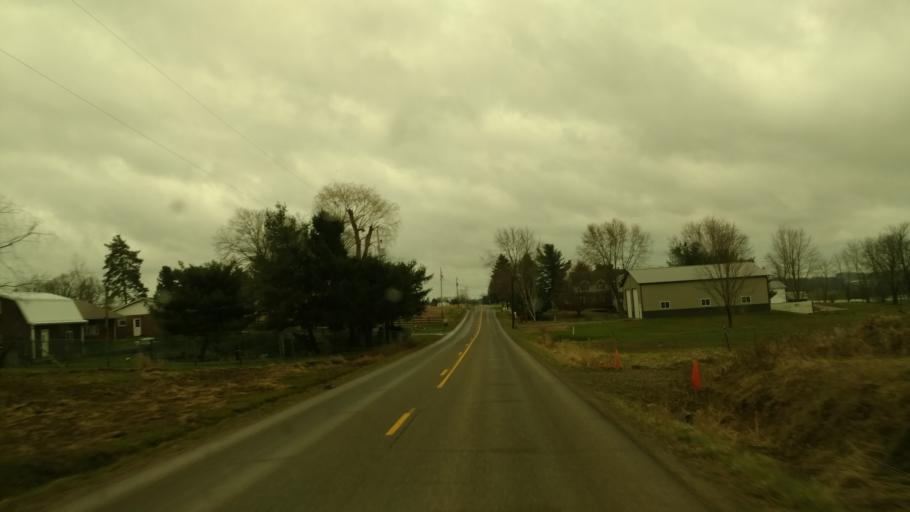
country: US
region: Ohio
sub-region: Holmes County
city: Millersburg
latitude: 40.5771
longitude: -81.8205
